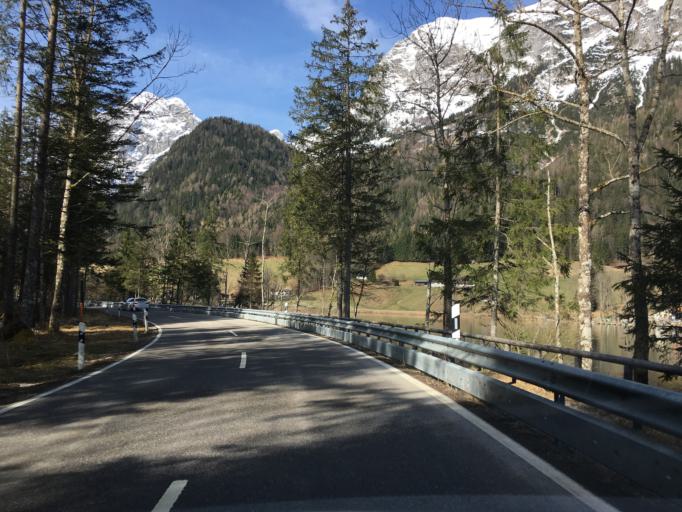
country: DE
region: Bavaria
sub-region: Upper Bavaria
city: Ramsau
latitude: 47.6055
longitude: 12.8555
